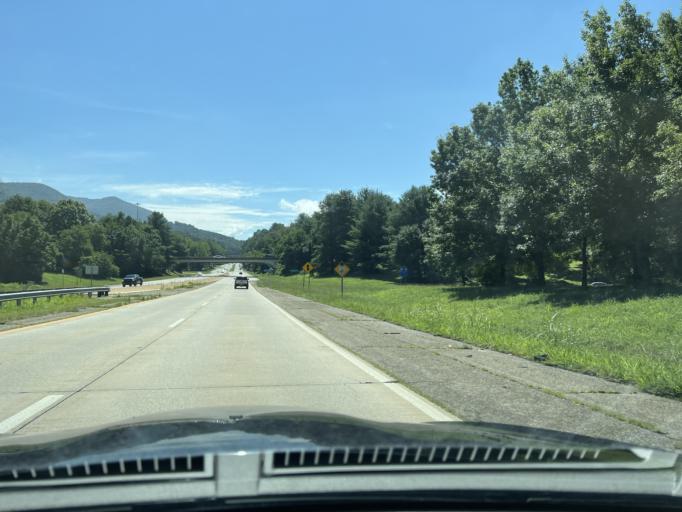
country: US
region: North Carolina
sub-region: Buncombe County
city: Biltmore Forest
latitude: 35.5655
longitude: -82.5014
